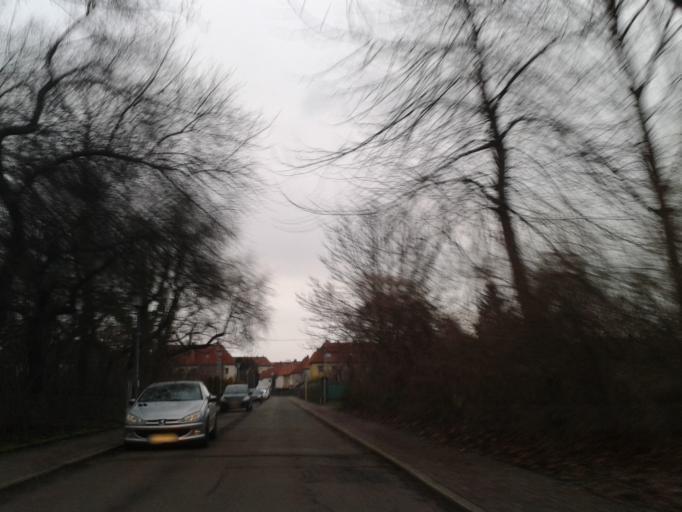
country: DE
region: Saxony-Anhalt
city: Halle Neustadt
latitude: 51.4596
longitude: 11.9566
